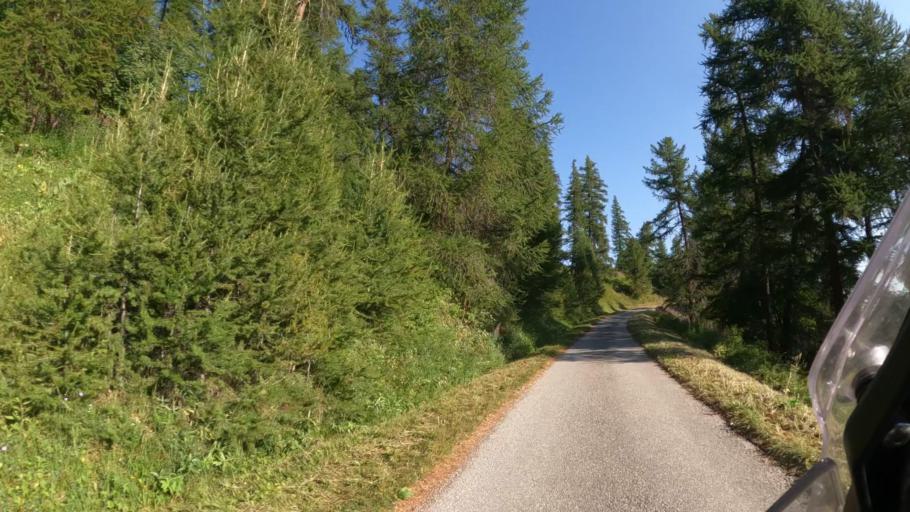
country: FR
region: Provence-Alpes-Cote d'Azur
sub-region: Departement des Hautes-Alpes
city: Guillestre
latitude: 44.6060
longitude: 6.6738
